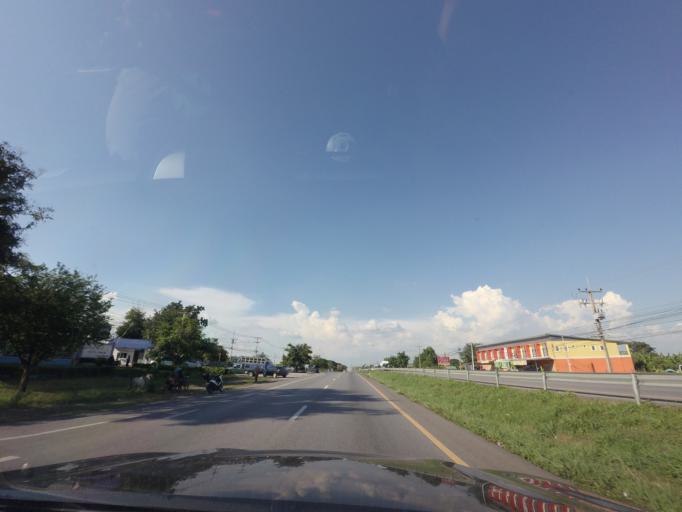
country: TH
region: Khon Kaen
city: Non Sila
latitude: 15.9773
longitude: 102.6947
